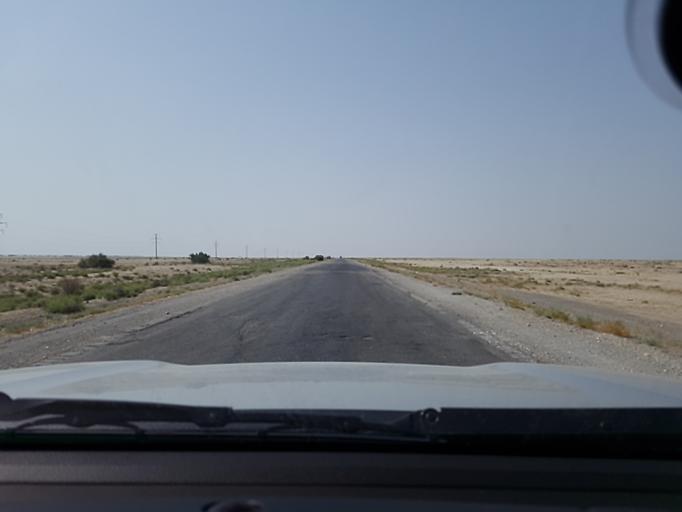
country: TM
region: Balkan
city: Gumdag
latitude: 38.8843
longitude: 54.5933
